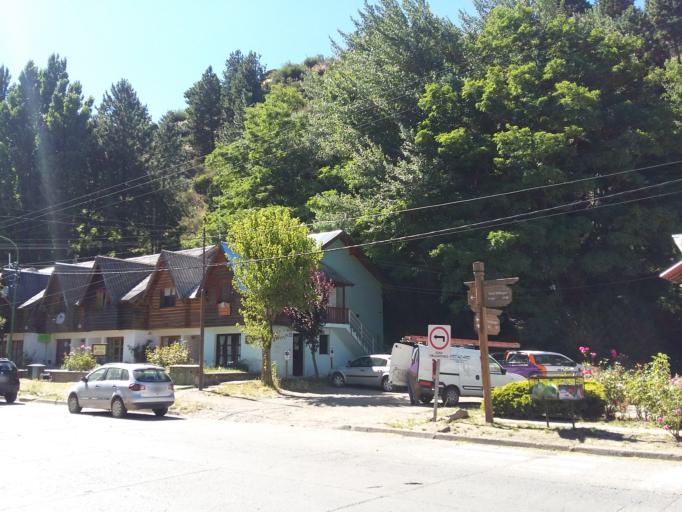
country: AR
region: Neuquen
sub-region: Departamento de Lacar
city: San Martin de los Andes
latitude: -40.1558
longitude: -71.3441
